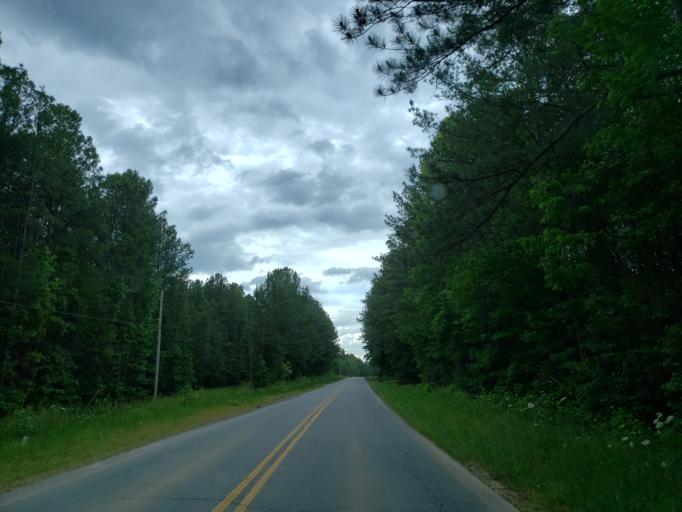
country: US
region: Georgia
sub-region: Polk County
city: Rockmart
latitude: 33.9322
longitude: -85.0535
